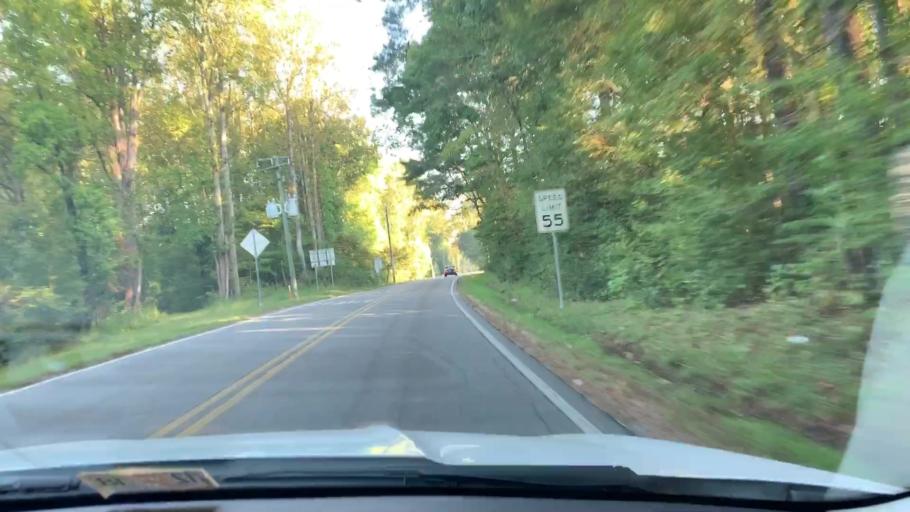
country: US
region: Virginia
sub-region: Gloucester County
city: Gloucester Courthouse
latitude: 37.4659
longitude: -76.4448
